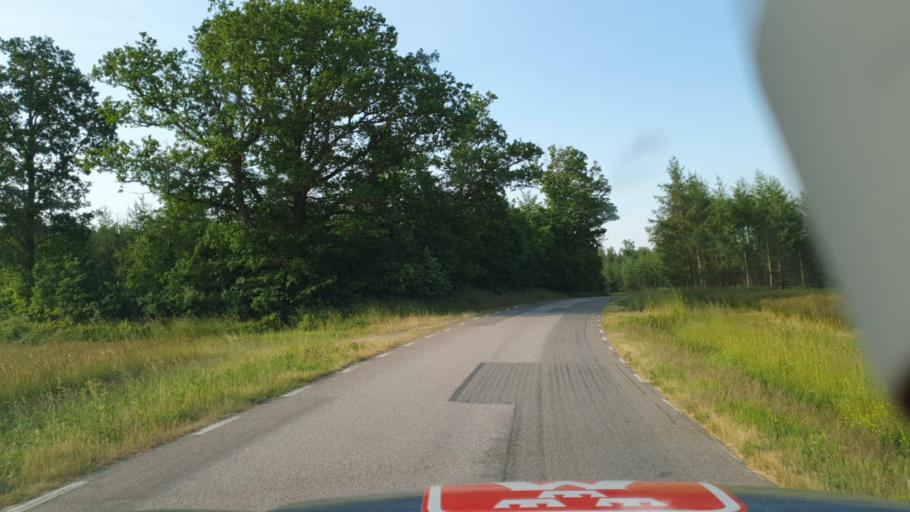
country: SE
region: Kalmar
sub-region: Torsas Kommun
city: Torsas
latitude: 56.4785
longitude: 16.0920
